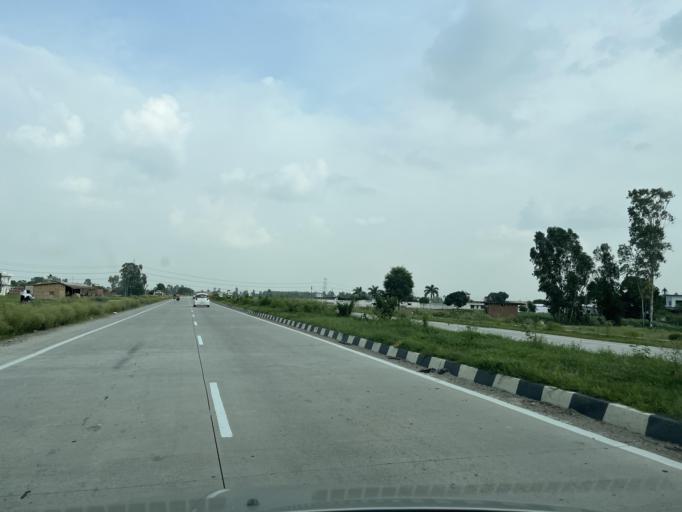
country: IN
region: Uttarakhand
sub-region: Udham Singh Nagar
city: Bazpur
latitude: 29.1501
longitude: 79.0749
